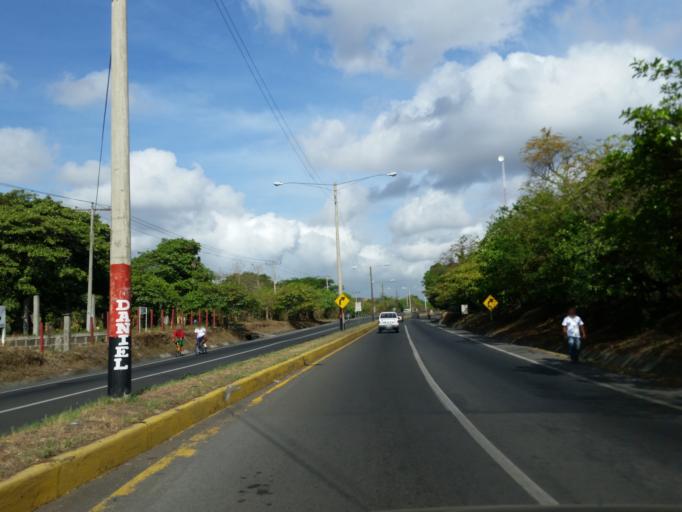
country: NI
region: Masaya
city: Nindiri
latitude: 11.9995
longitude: -86.1263
